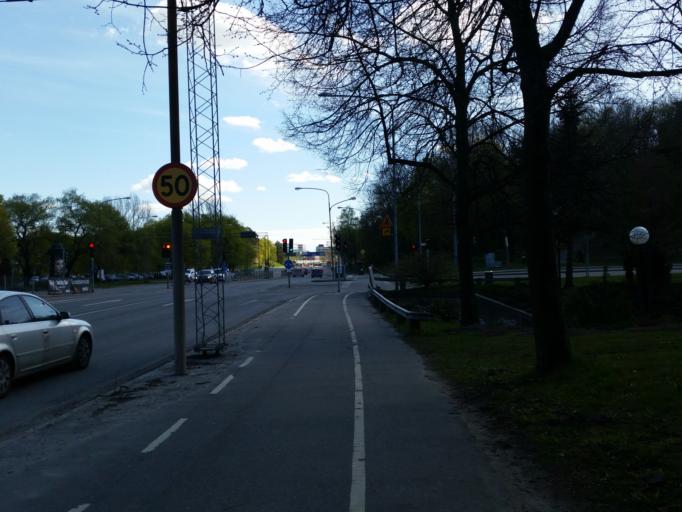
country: SE
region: Stockholm
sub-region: Solna Kommun
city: Solna
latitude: 59.3593
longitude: 18.0037
